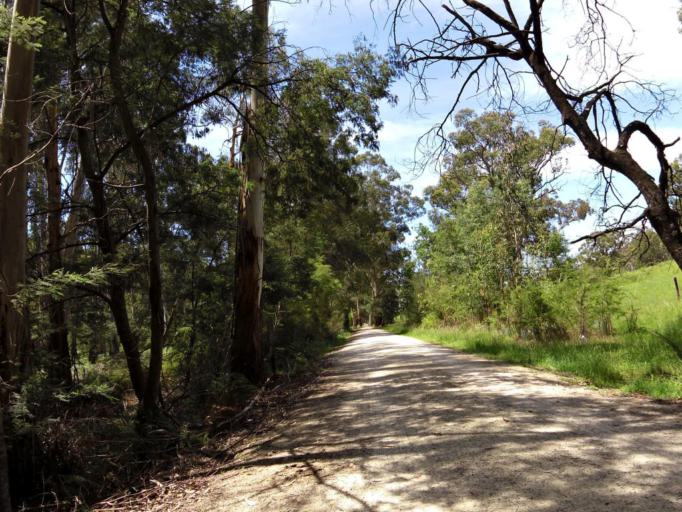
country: AU
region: Victoria
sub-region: Yarra Ranges
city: Woori Yallock
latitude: -37.7586
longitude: 145.4724
